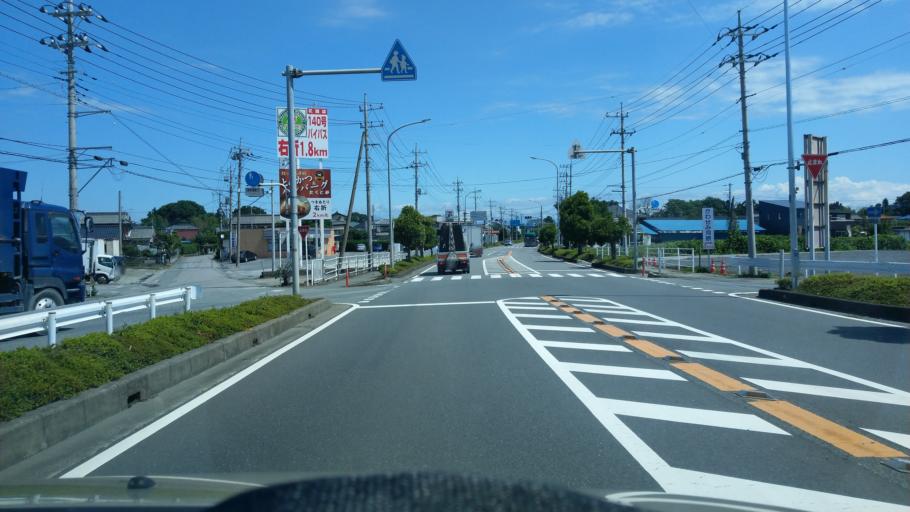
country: JP
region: Saitama
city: Yorii
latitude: 36.1162
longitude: 139.2106
